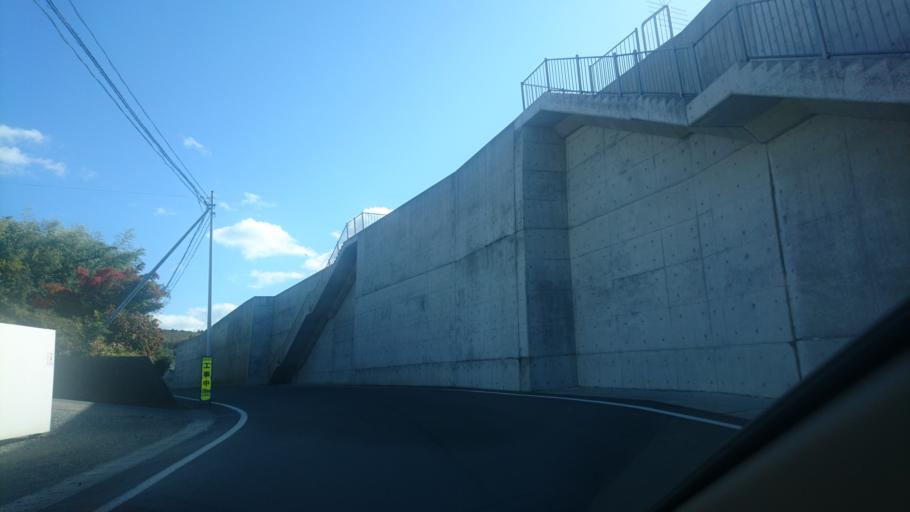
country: JP
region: Iwate
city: Ofunato
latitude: 38.9982
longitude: 141.7170
